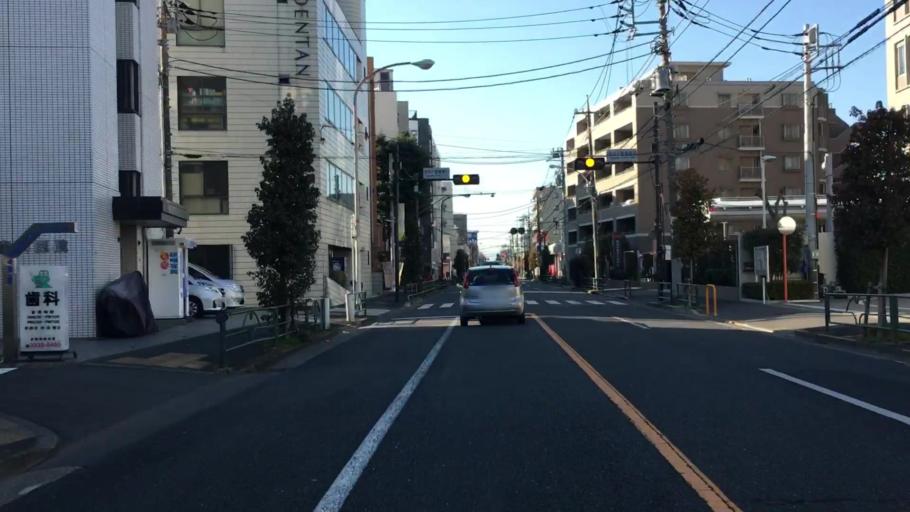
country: JP
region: Tokyo
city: Mitaka-shi
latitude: 35.6903
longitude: 139.6118
